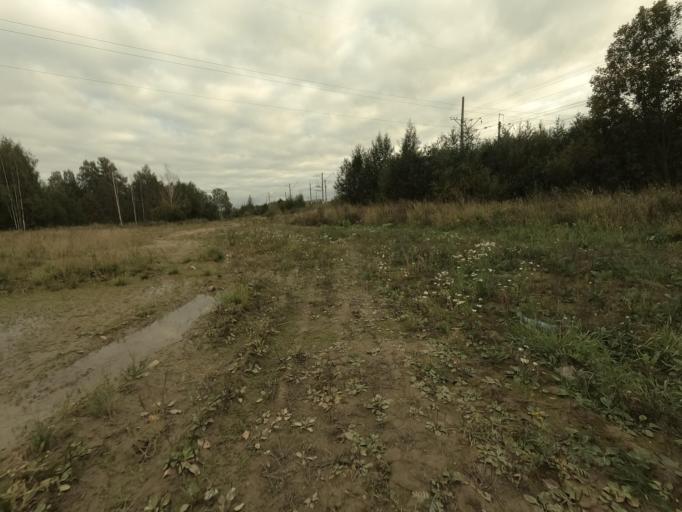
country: RU
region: St.-Petersburg
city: Metallostroy
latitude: 59.8211
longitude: 30.5296
